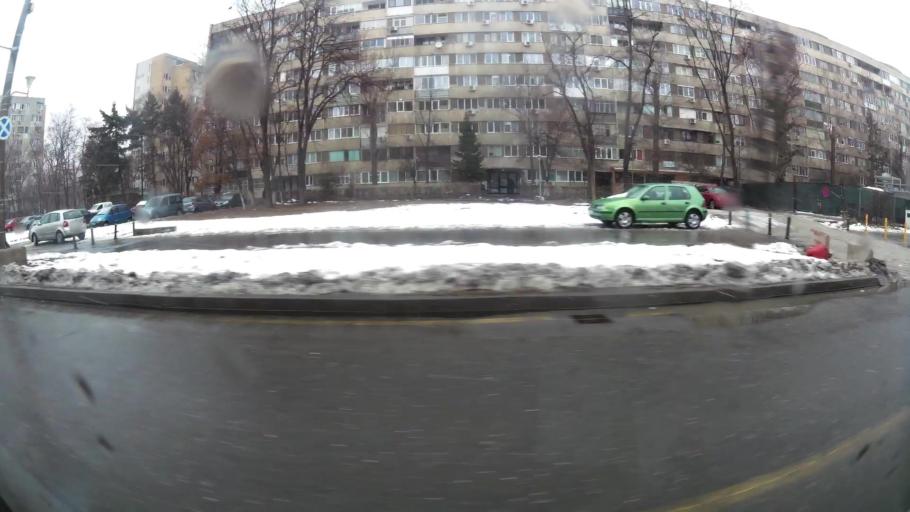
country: RO
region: Ilfov
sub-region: Comuna Chiajna
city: Rosu
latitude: 44.4250
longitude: 26.0490
